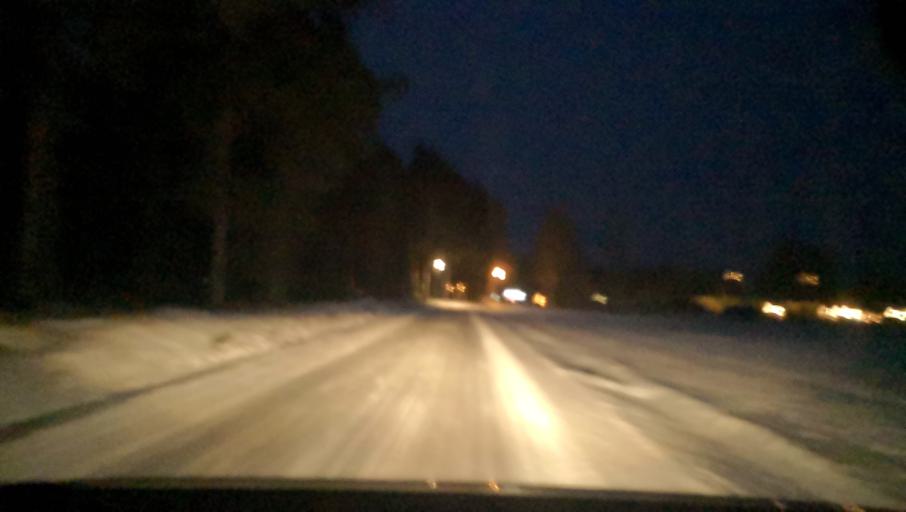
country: SE
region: Uppsala
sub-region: Heby Kommun
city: Tarnsjo
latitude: 60.2975
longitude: 16.8056
